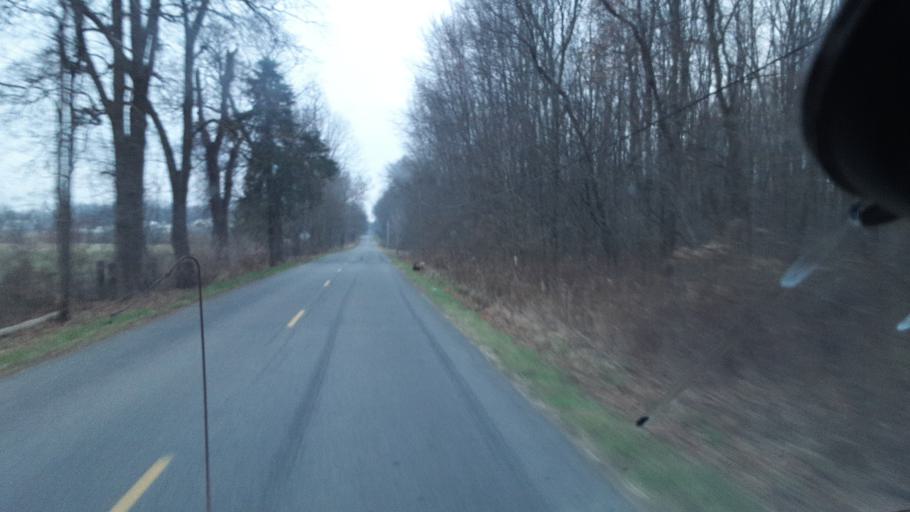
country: US
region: Indiana
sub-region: Elkhart County
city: Bristol
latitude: 41.6656
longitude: -85.7874
